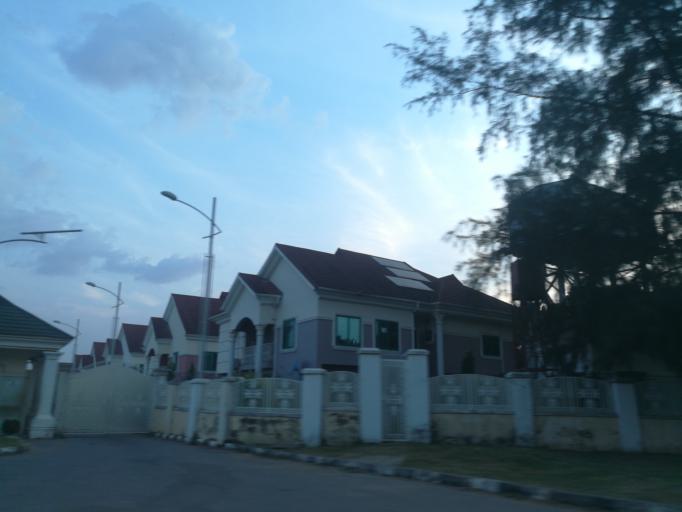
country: NG
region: Abuja Federal Capital Territory
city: Abuja
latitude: 9.0718
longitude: 7.4028
